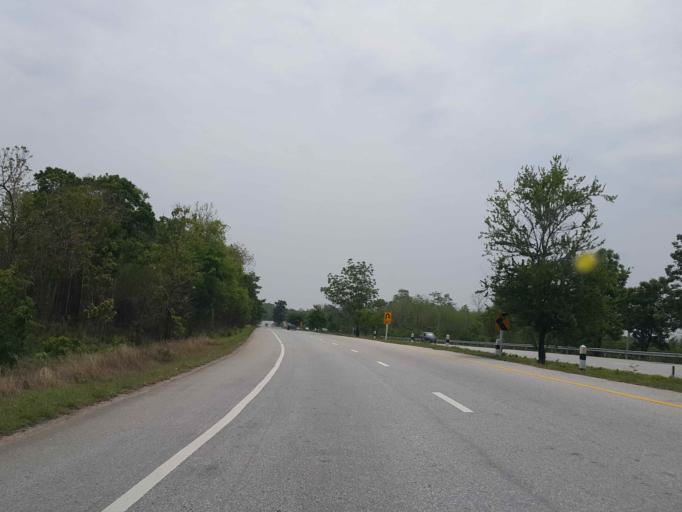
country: TH
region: Lampang
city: Sop Prap
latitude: 17.7756
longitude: 99.2500
